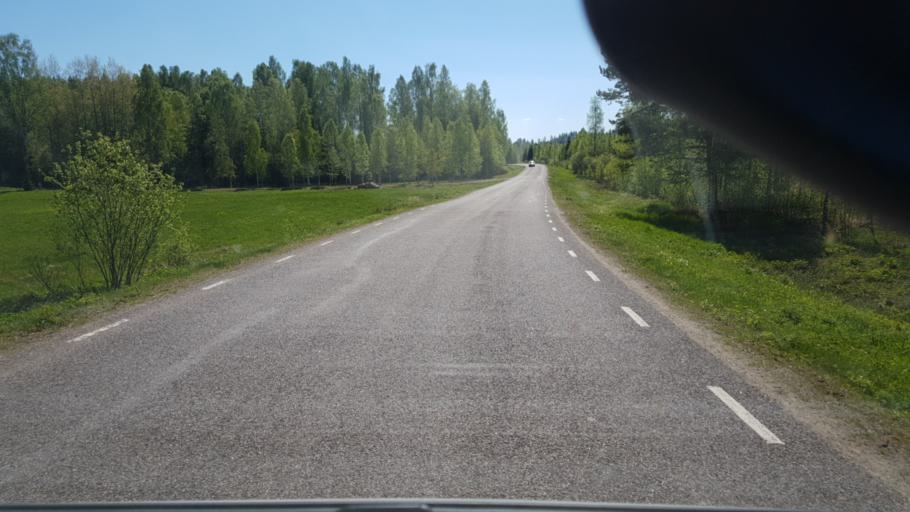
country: SE
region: Vaermland
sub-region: Eda Kommun
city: Charlottenberg
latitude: 59.9724
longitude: 12.4112
